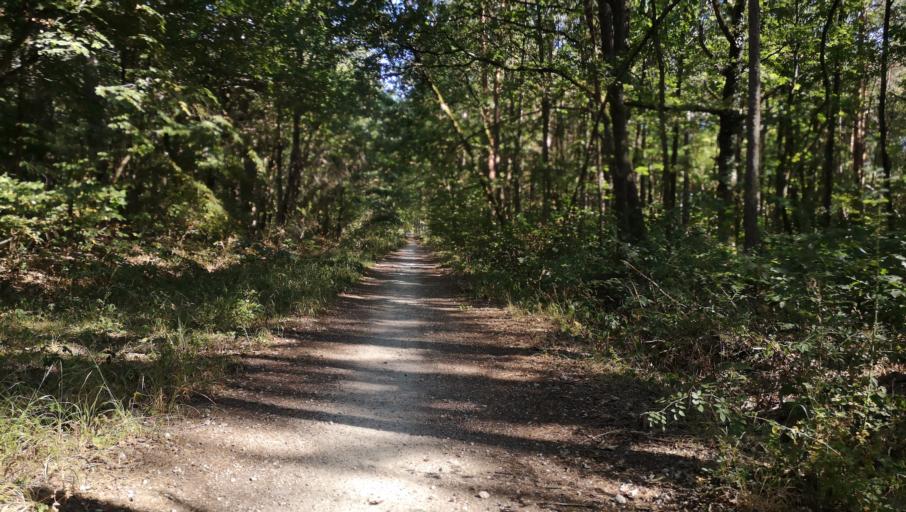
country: FR
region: Centre
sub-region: Departement du Loiret
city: Saran
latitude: 47.9620
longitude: 1.8939
